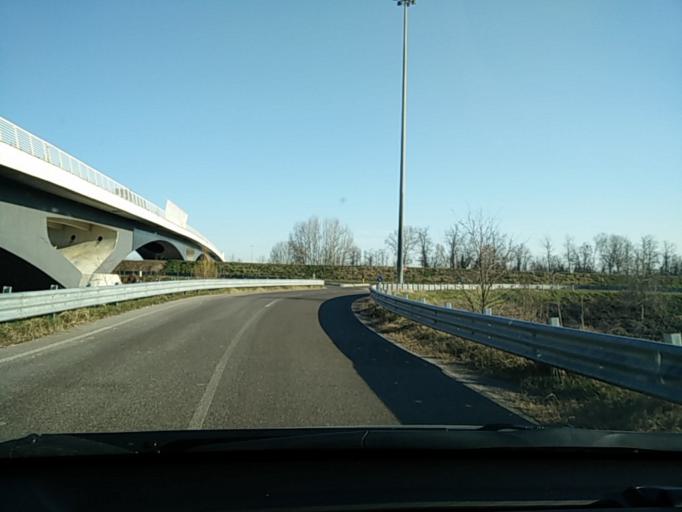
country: IT
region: Veneto
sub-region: Provincia di Venezia
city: Passarella
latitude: 45.6043
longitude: 12.5955
